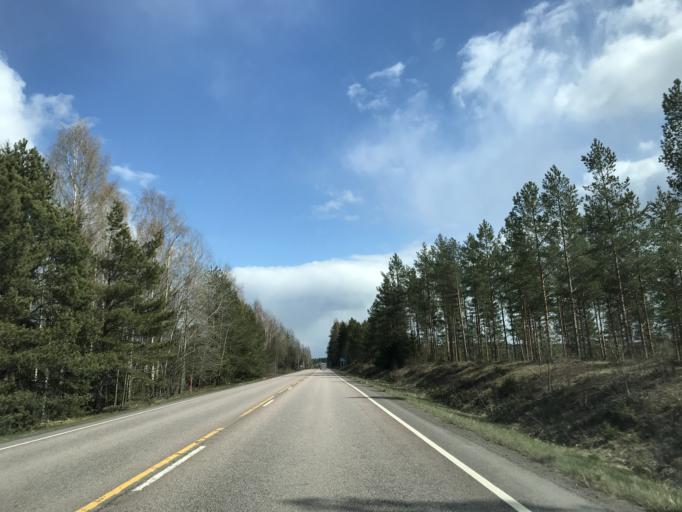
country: FI
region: Uusimaa
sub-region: Helsinki
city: Hyvinge
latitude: 60.5412
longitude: 24.8865
